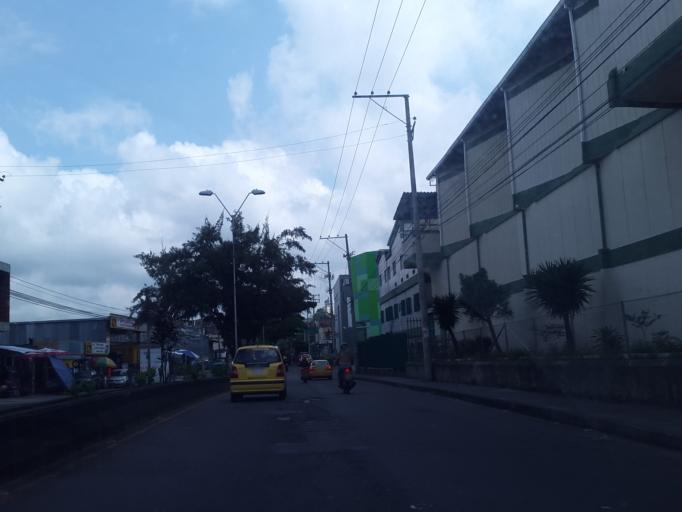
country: CO
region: Quindio
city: Armenia
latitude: 4.5438
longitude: -75.6706
